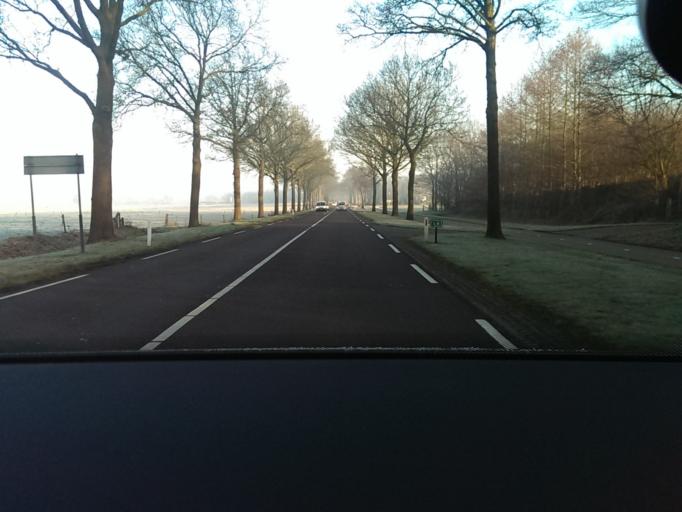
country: NL
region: Overijssel
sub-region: Gemeente Twenterand
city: Vroomshoop
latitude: 52.4146
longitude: 6.5536
